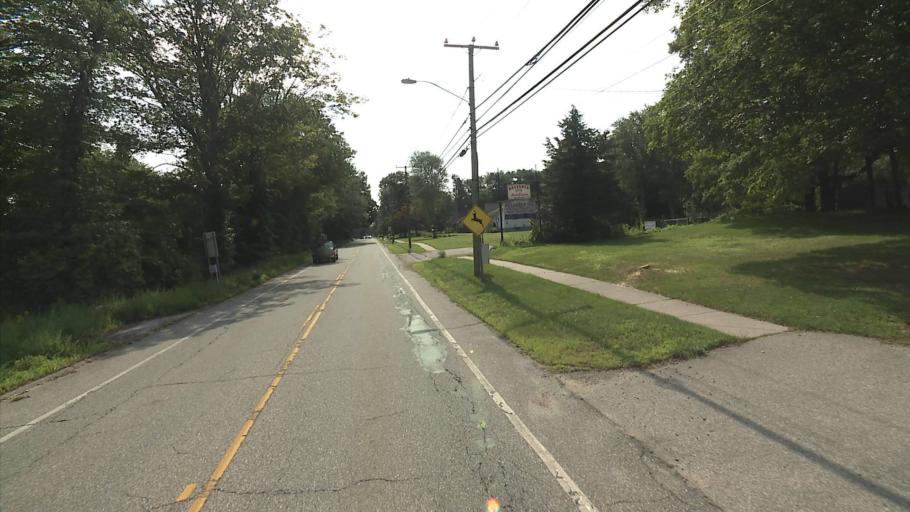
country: US
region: Connecticut
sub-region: New London County
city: Colchester
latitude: 41.5746
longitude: -72.3141
